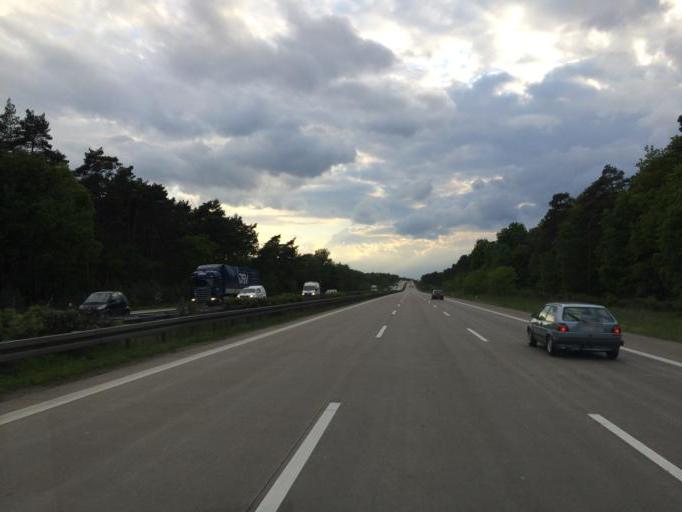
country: DE
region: Saxony-Anhalt
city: Burg bei Magdeburg
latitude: 52.2288
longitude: 11.8593
